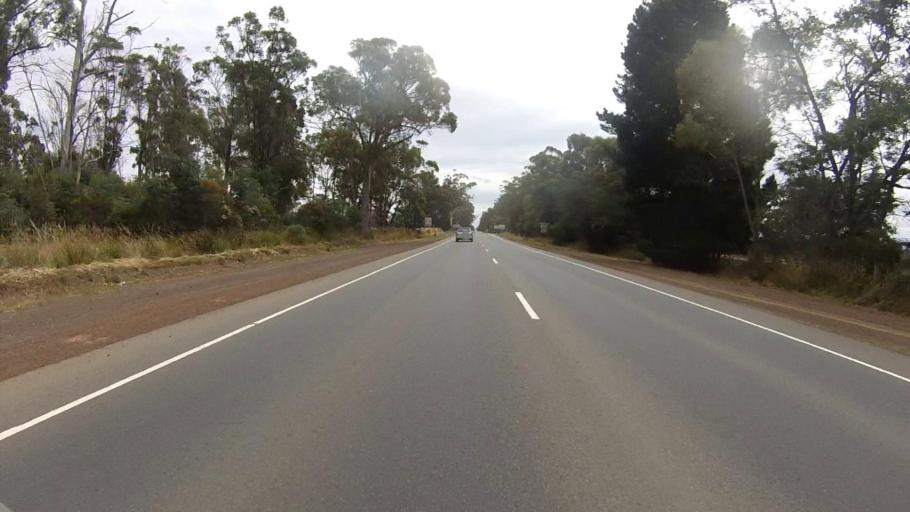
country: AU
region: Tasmania
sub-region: Northern Midlands
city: Evandale
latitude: -41.7576
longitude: 147.3489
